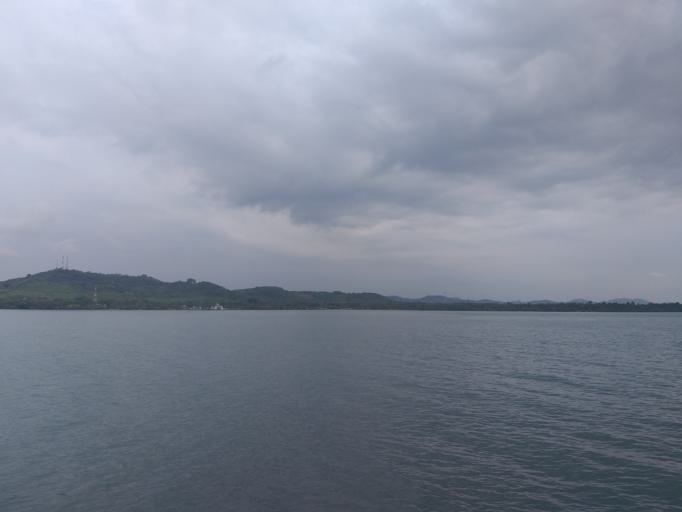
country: TH
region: Trat
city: Laem Ngop
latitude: 12.1727
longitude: 102.2981
